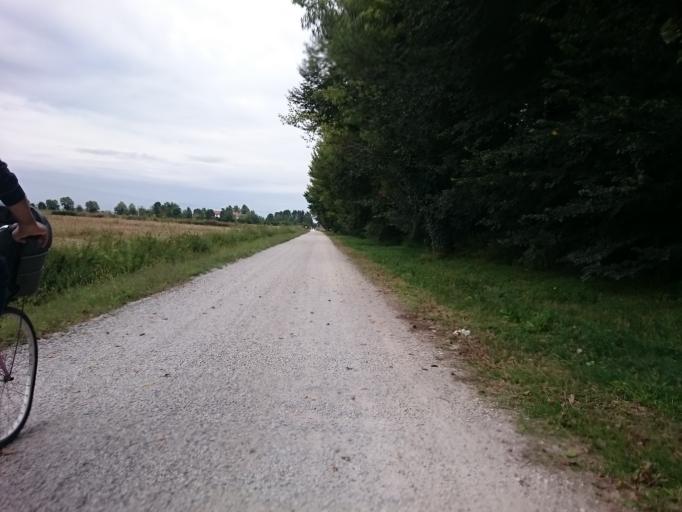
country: IT
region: Veneto
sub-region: Provincia di Vicenza
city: Grumolo delle Abbadesse
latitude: 45.4985
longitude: 11.6594
